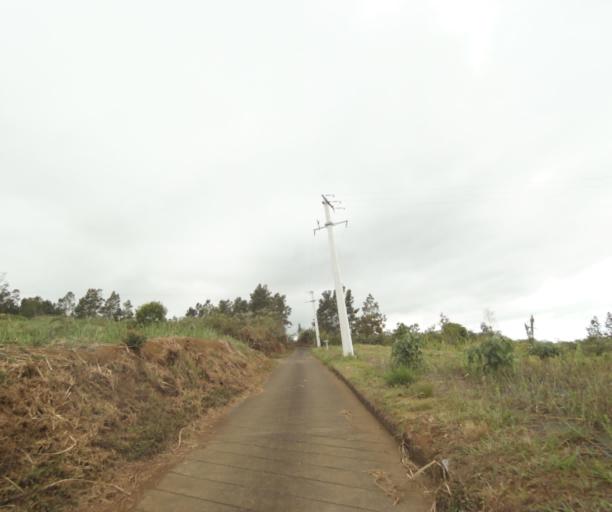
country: RE
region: Reunion
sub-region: Reunion
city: Saint-Paul
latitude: -21.0078
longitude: 55.3487
